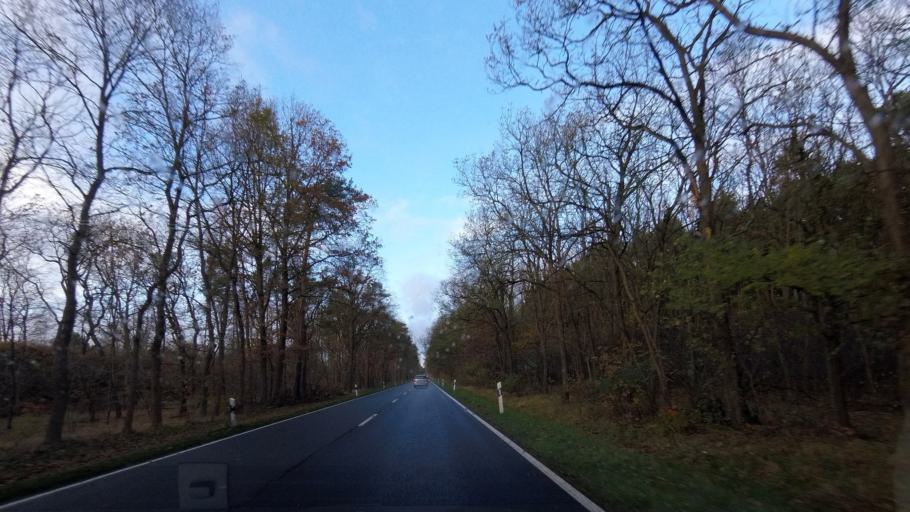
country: DE
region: Brandenburg
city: Treuenbrietzen
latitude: 52.0607
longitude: 12.8997
